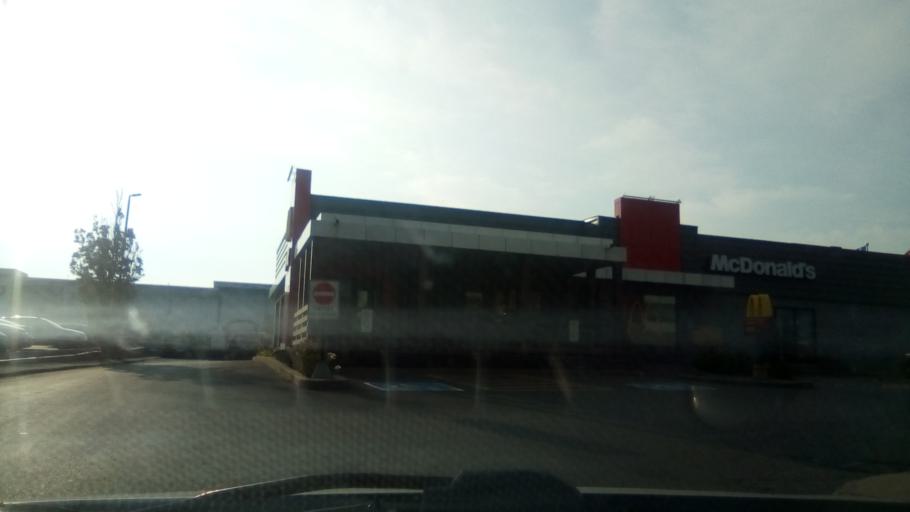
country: CA
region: Quebec
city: Mont-Royal
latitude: 45.5206
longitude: -73.6257
